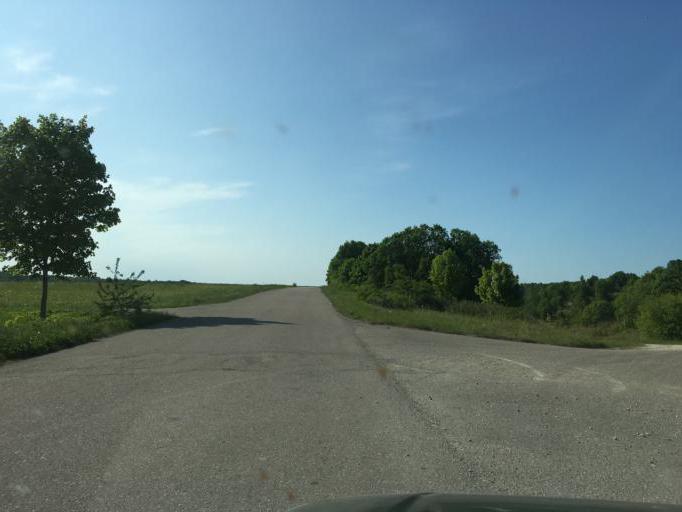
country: LV
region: Dundaga
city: Dundaga
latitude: 57.6098
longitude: 22.4424
